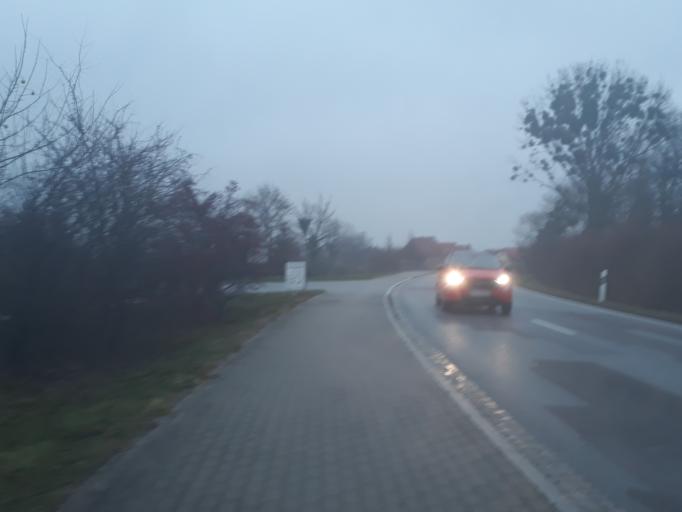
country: DE
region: Saxony
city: Guttau
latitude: 51.2585
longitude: 14.5556
